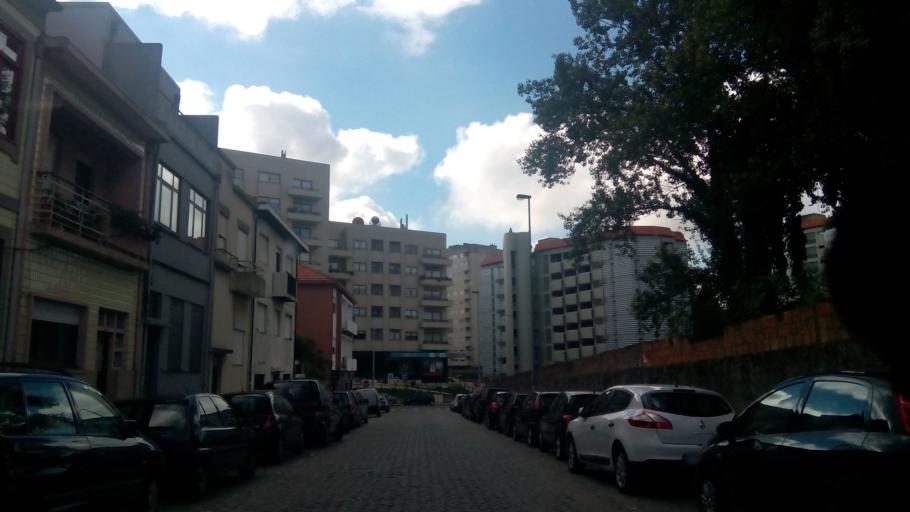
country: PT
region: Porto
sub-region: Porto
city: Porto
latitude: 41.1638
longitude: -8.6003
